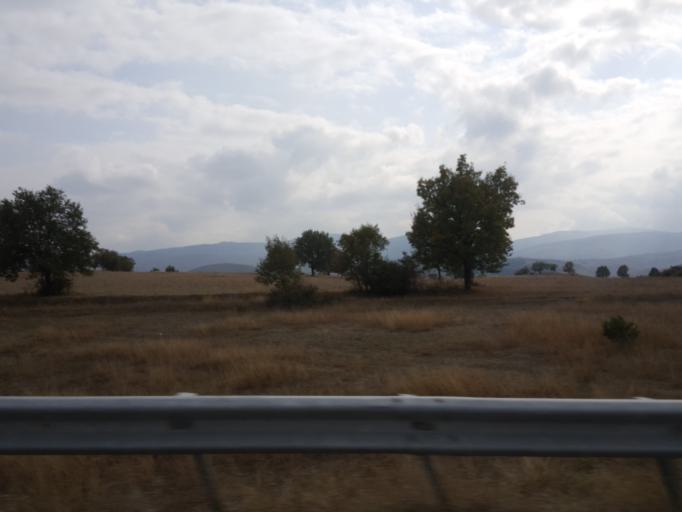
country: TR
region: Sinop
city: Sarayduzu
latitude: 41.3341
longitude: 34.7806
